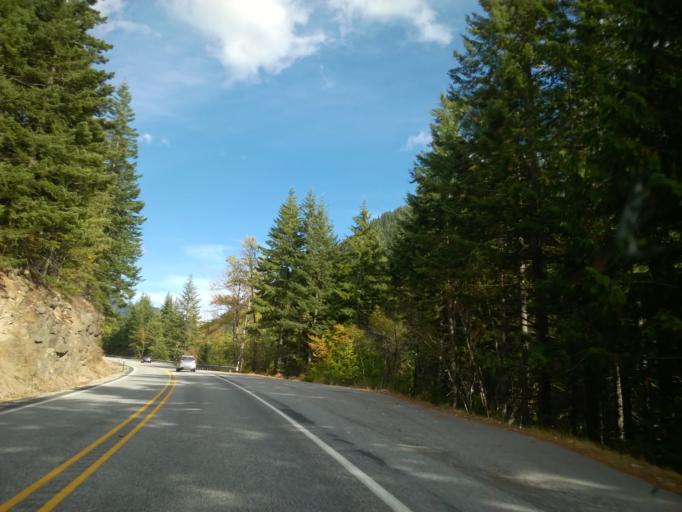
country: US
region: Washington
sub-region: Chelan County
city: Leavenworth
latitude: 47.7760
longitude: -120.9513
